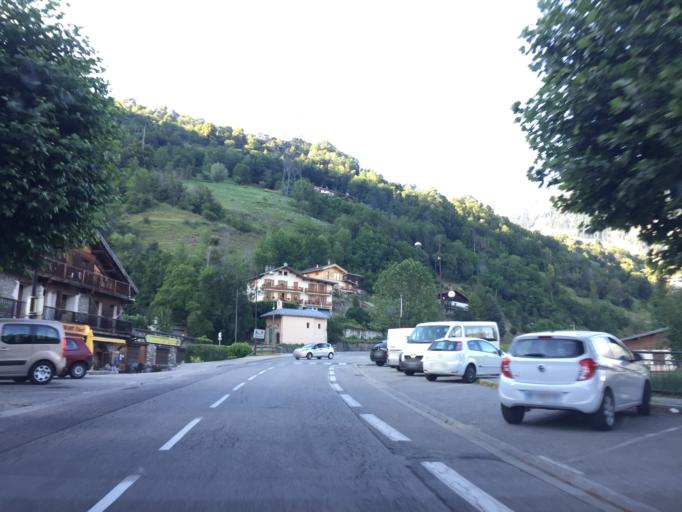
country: FR
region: Rhone-Alpes
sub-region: Departement de la Savoie
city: Bourg-Saint-Maurice
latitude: 45.6223
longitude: 6.7709
